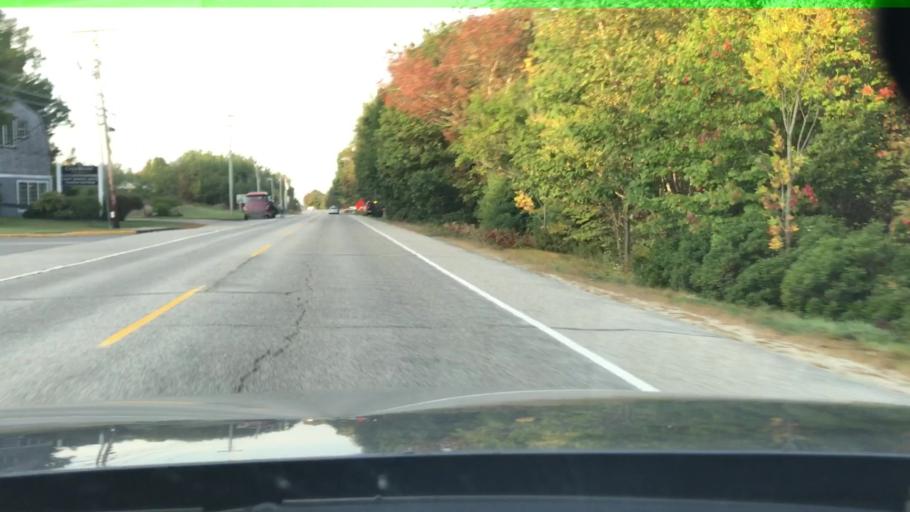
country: US
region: Maine
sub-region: Cumberland County
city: Freeport
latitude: 43.8354
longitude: -70.1267
